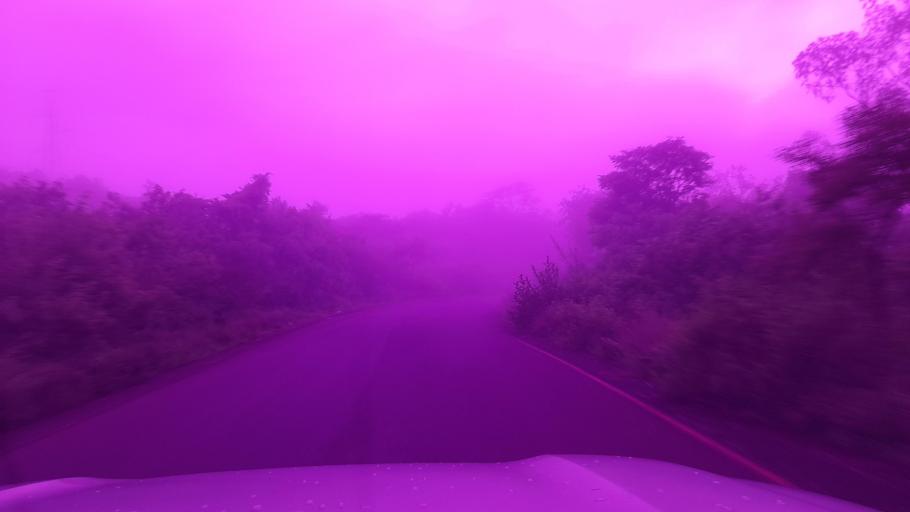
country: ET
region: Oromiya
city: Waliso
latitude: 8.1755
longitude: 37.5553
